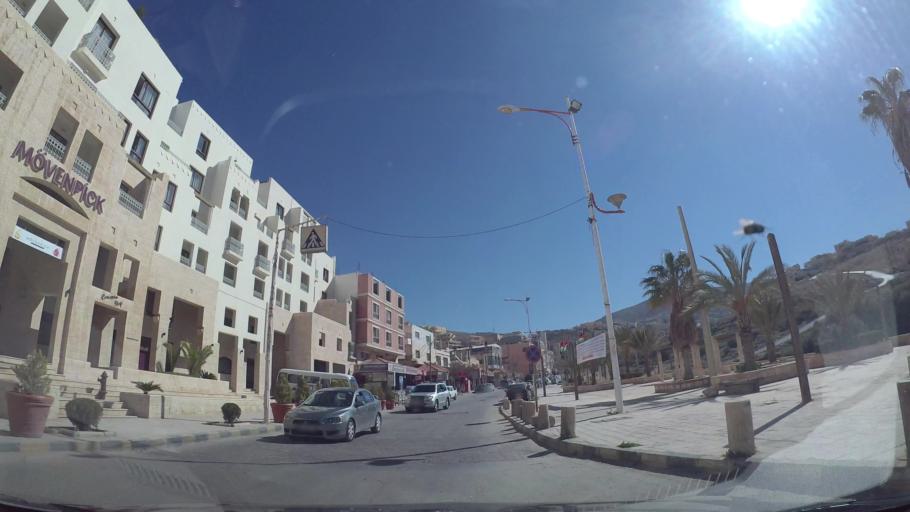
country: JO
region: Ma'an
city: Petra
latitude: 30.3250
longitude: 35.4694
